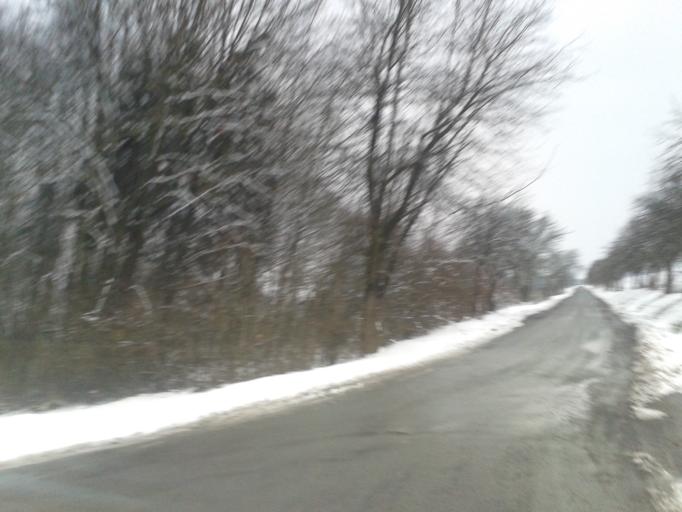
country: CZ
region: Central Bohemia
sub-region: Okres Beroun
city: Lodenice
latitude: 49.9123
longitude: 14.1529
